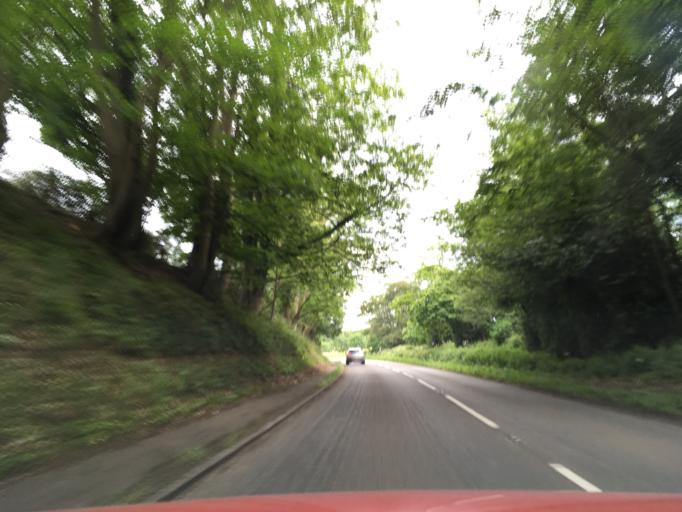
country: GB
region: England
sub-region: Central Bedfordshire
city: Aspley Guise
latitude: 51.9965
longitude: -0.6333
